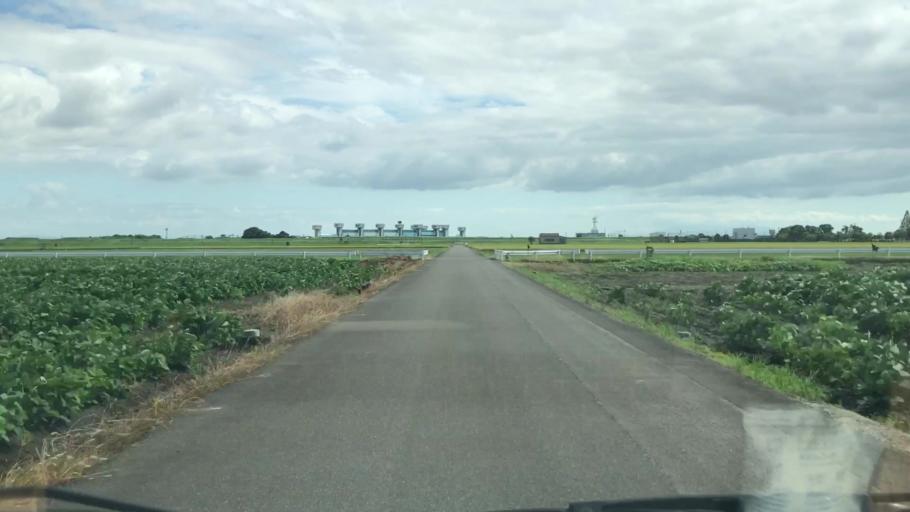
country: JP
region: Saga Prefecture
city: Saga-shi
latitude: 33.2119
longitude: 130.1841
